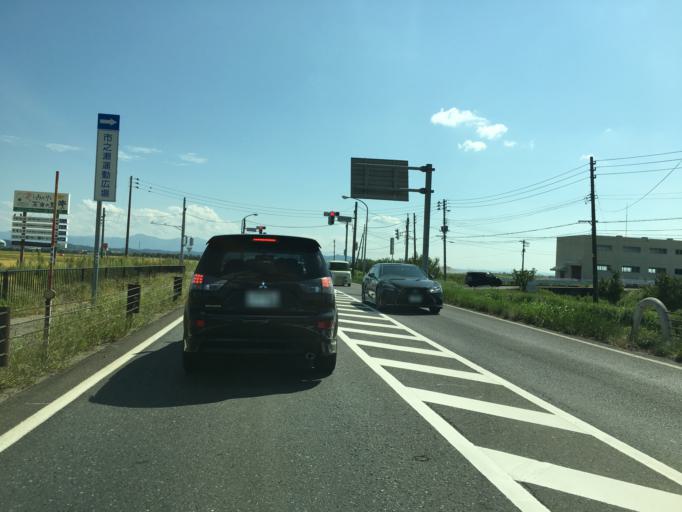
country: JP
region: Niigata
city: Niitsu-honcho
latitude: 37.8327
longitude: 139.0968
